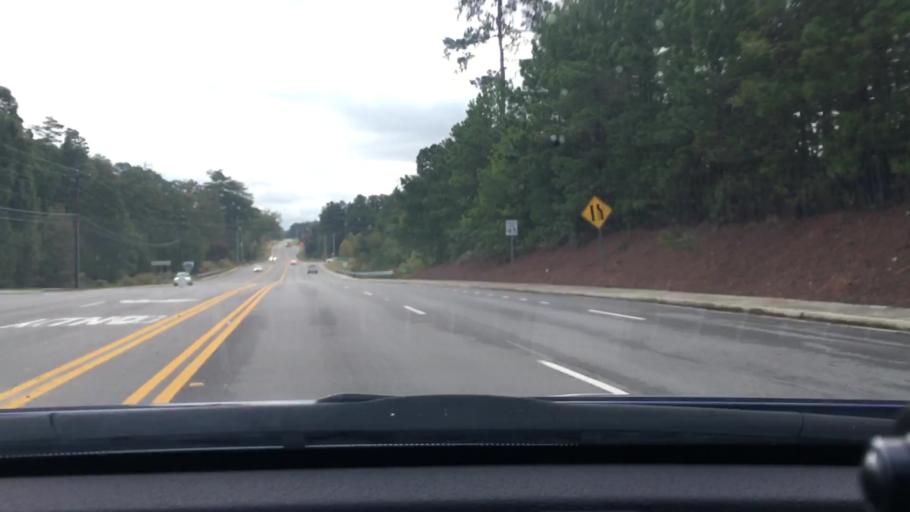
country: US
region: South Carolina
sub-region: Lexington County
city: Irmo
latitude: 34.0899
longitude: -81.1602
